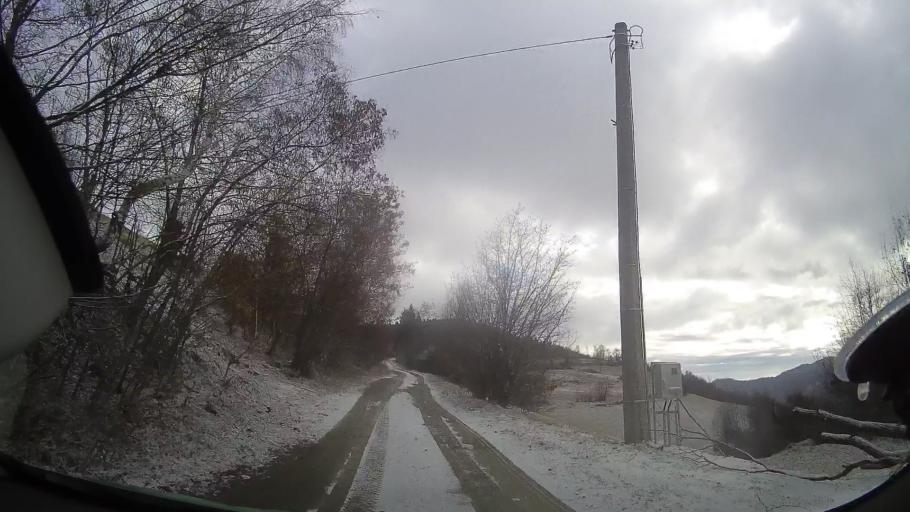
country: RO
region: Cluj
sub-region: Comuna Valea Ierii
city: Valea Ierii
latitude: 46.6491
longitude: 23.3549
